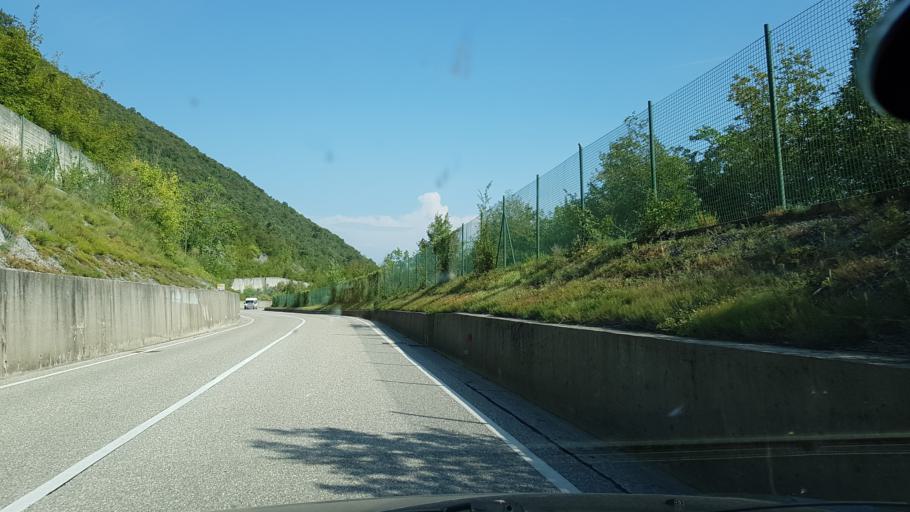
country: SI
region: Nova Gorica
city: Solkan
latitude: 45.9826
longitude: 13.6293
